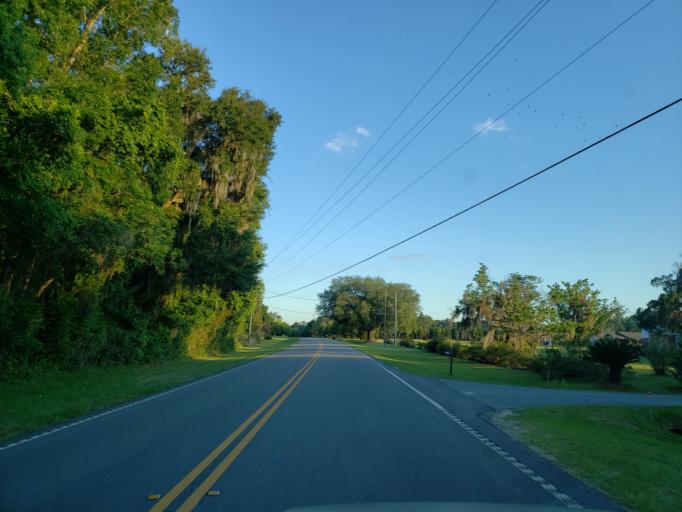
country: US
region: Georgia
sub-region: Lowndes County
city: Valdosta
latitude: 30.7376
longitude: -83.2511
